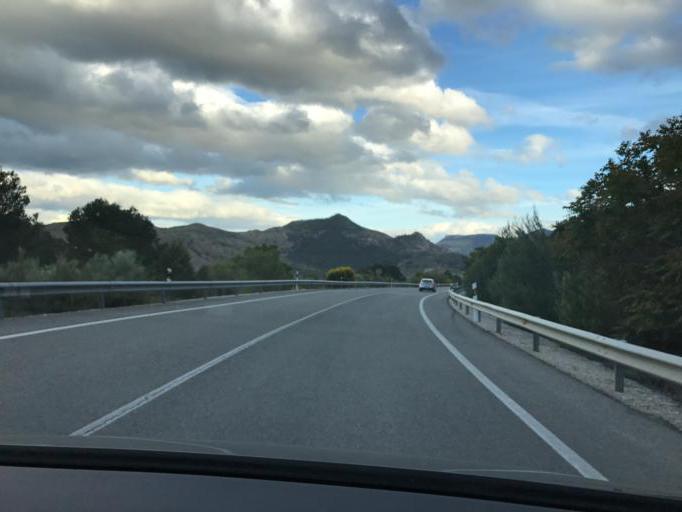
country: ES
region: Andalusia
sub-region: Provincia de Jaen
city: Belmez de la Moraleda
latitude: 37.7708
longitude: -3.3366
